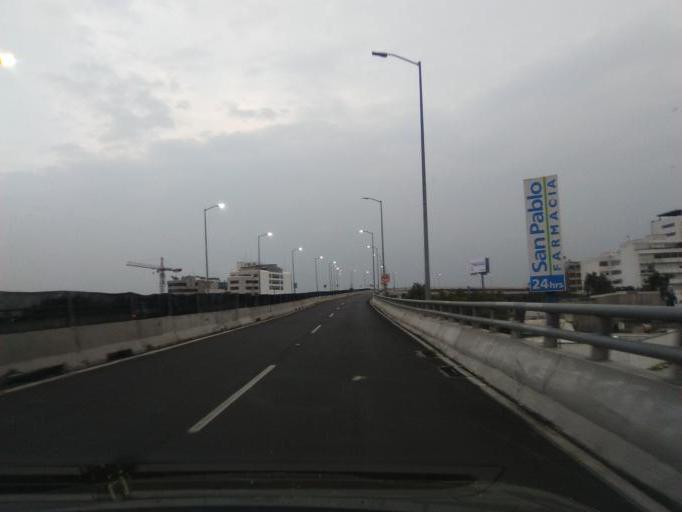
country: MX
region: Mexico City
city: Magdalena Contreras
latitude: 19.3229
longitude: -99.2232
